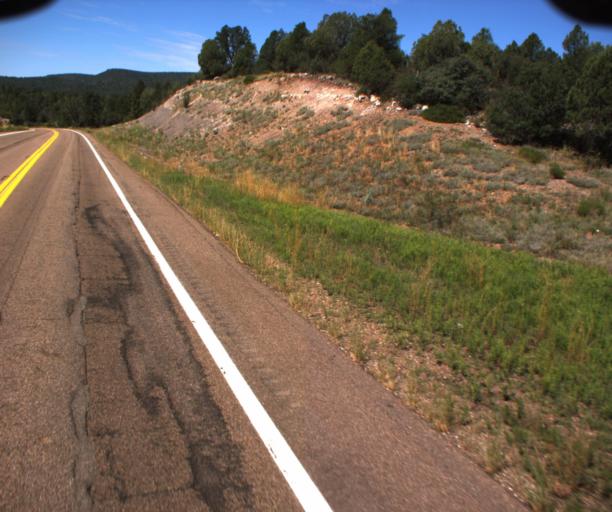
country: US
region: Arizona
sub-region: Navajo County
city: Cibecue
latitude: 33.8665
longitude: -110.4108
